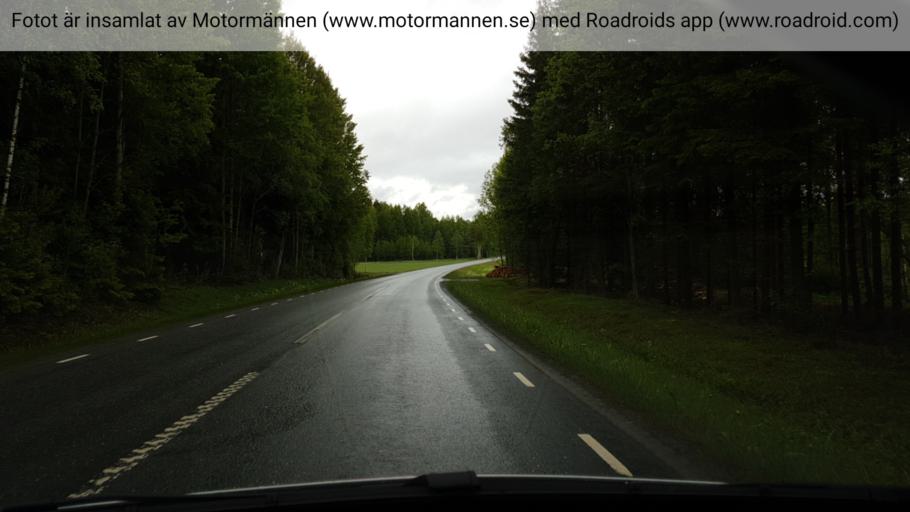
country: SE
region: Joenkoeping
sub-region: Aneby Kommun
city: Aneby
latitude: 57.7994
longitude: 14.7000
